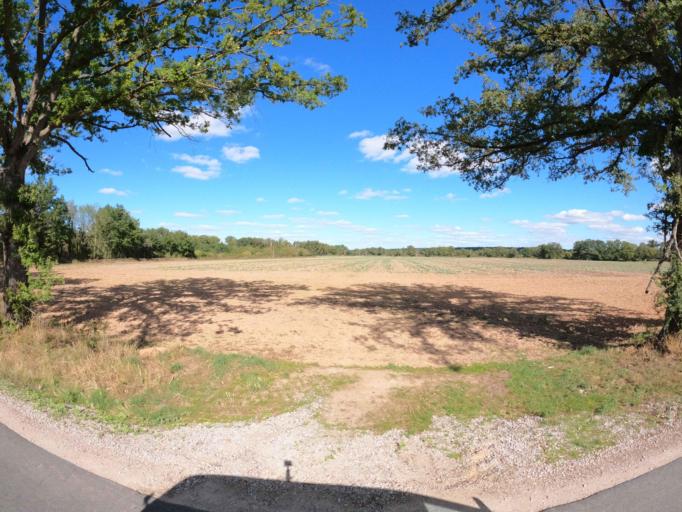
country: FR
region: Auvergne
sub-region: Departement de l'Allier
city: Doyet
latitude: 46.3938
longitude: 2.7548
